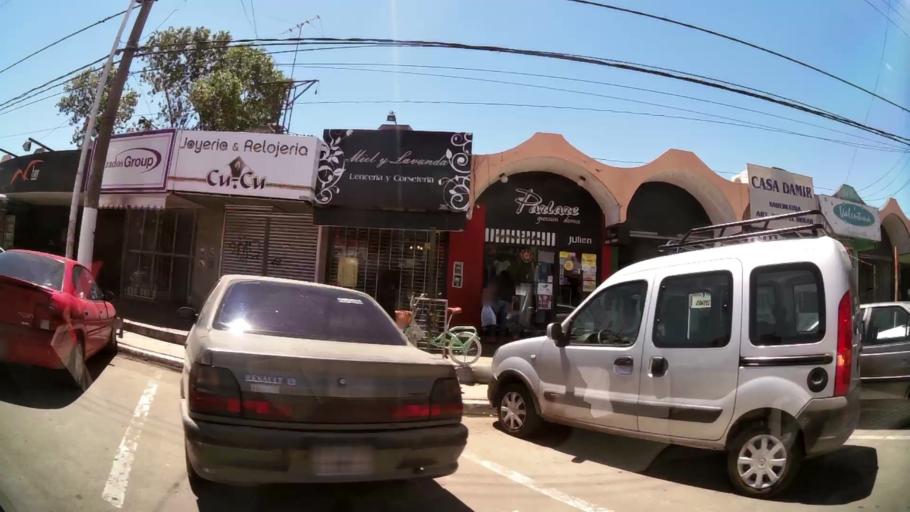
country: AR
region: Buenos Aires
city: Hurlingham
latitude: -34.4999
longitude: -58.6938
